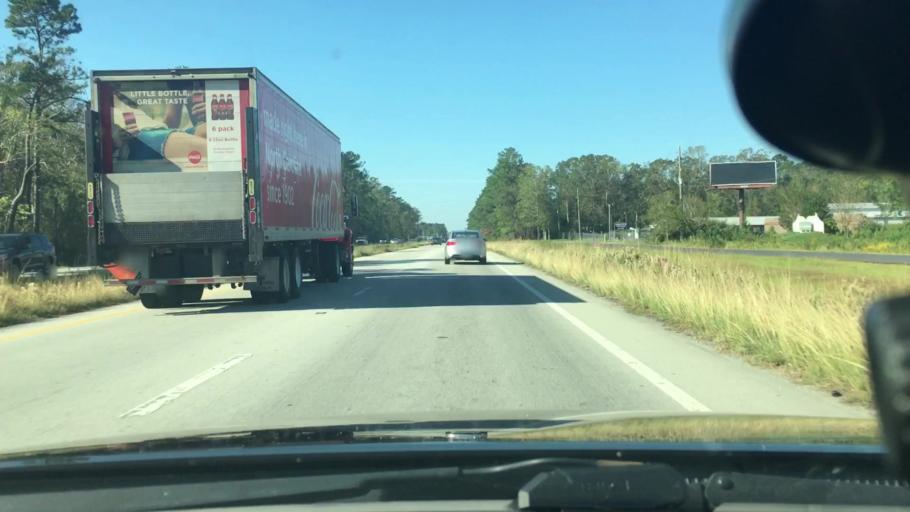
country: US
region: North Carolina
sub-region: Craven County
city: James City
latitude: 35.0394
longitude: -77.0079
